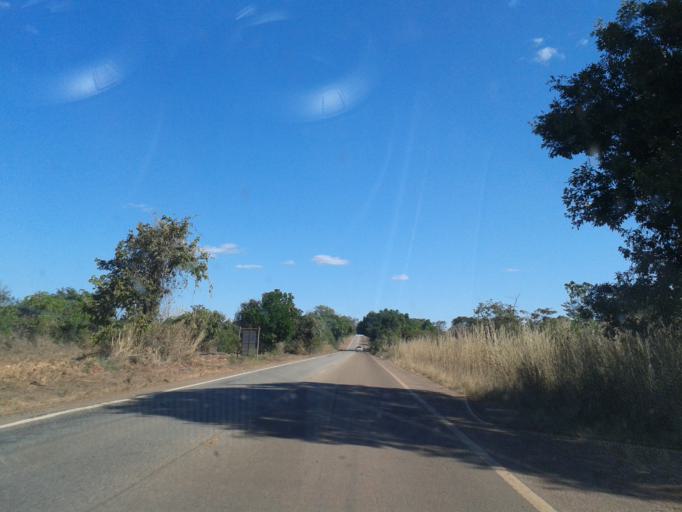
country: BR
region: Goias
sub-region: Mozarlandia
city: Mozarlandia
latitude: -14.4050
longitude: -50.4445
